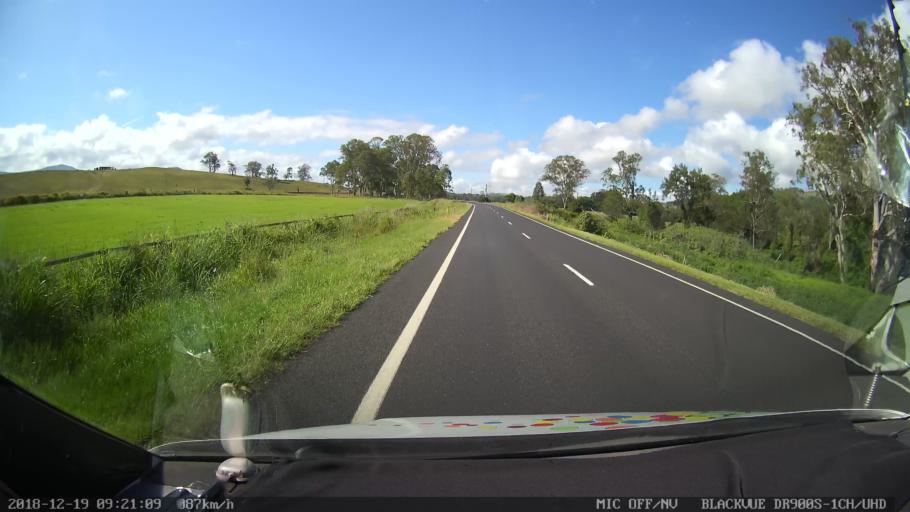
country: AU
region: New South Wales
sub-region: Kyogle
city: Kyogle
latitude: -28.5800
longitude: 152.9822
